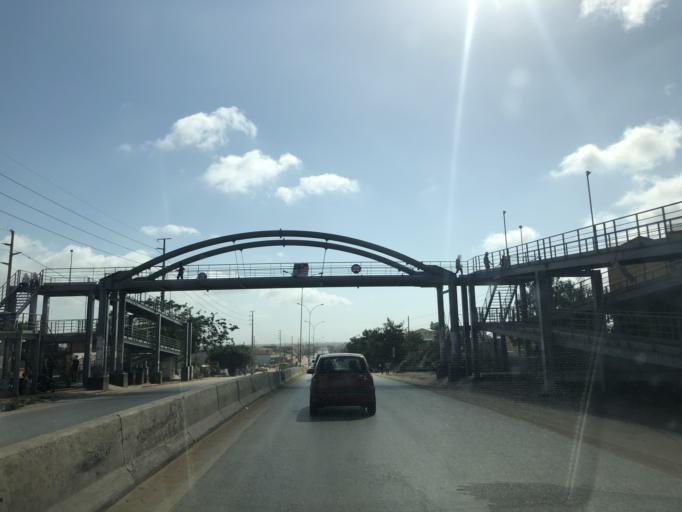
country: AO
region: Luanda
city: Luanda
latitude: -8.9084
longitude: 13.2409
